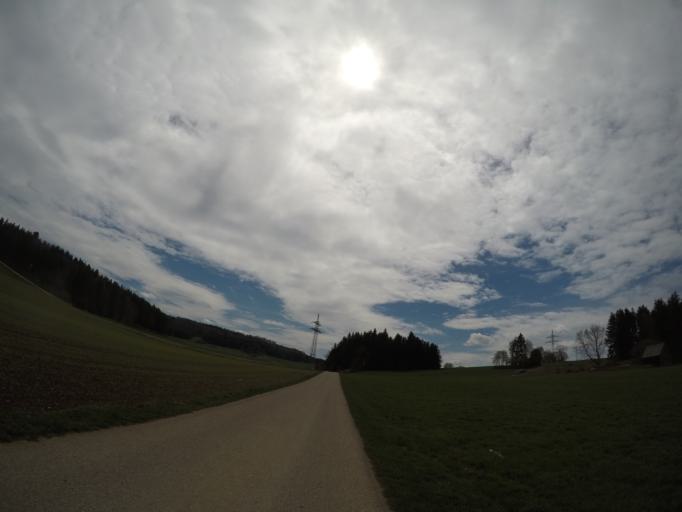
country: DE
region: Baden-Wuerttemberg
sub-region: Tuebingen Region
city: Laichingen
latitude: 48.4889
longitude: 9.6535
